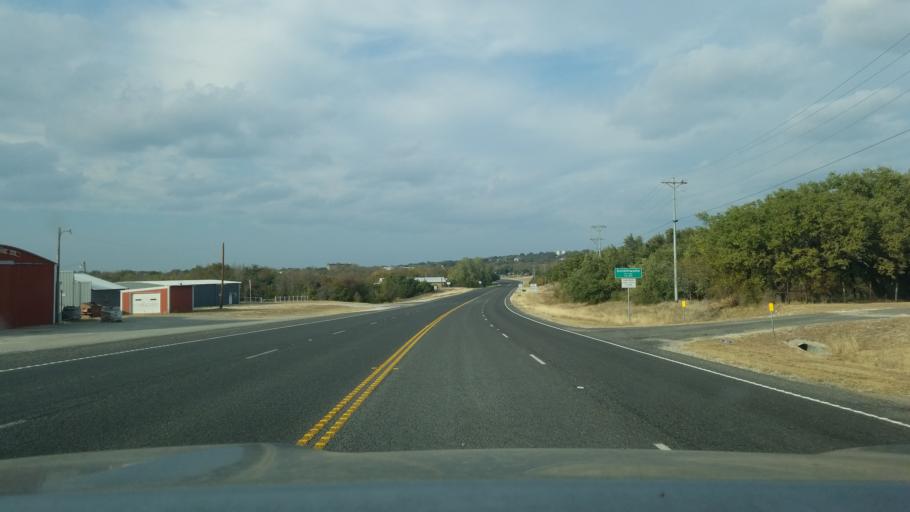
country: US
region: Texas
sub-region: Mills County
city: Goldthwaite
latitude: 31.4392
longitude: -98.5683
